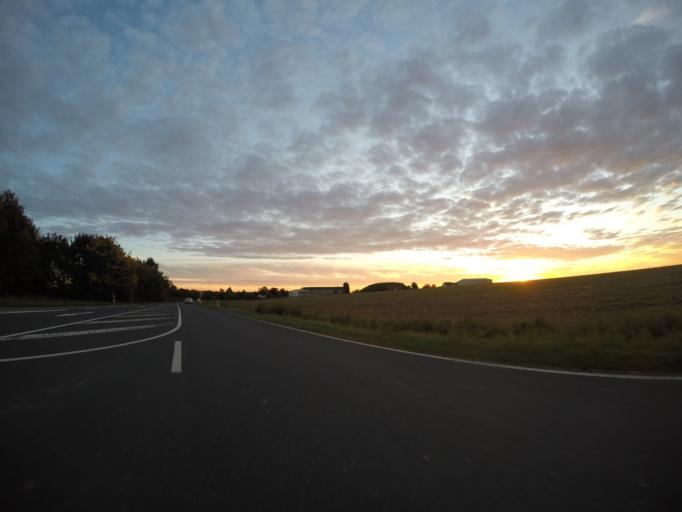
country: DE
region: Rheinland-Pfalz
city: Meinborn
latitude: 50.5000
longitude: 7.5610
